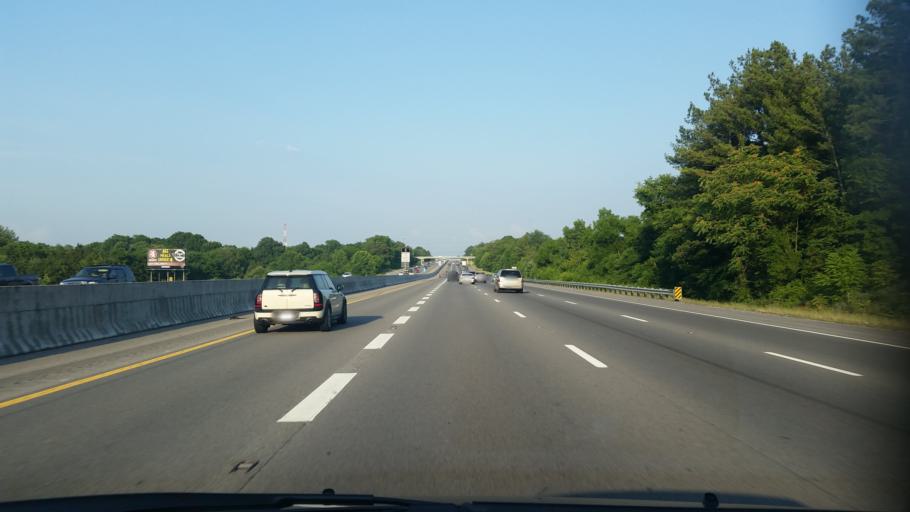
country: US
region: Tennessee
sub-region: Wilson County
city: Green Hill
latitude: 36.1700
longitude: -86.5933
